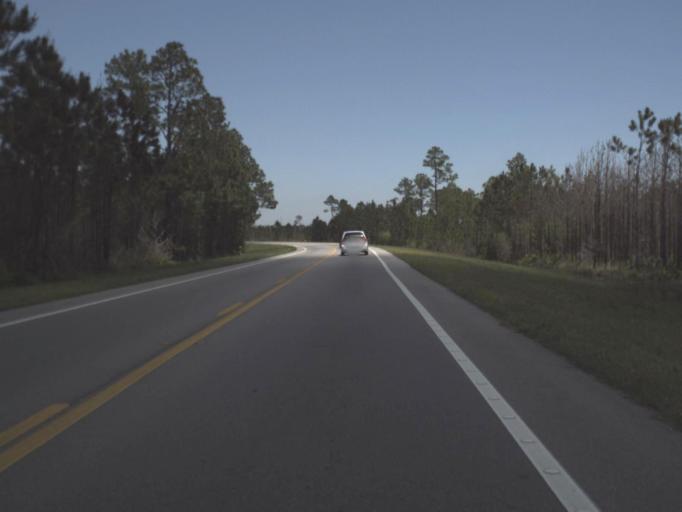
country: US
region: Florida
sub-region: Escambia County
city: Myrtle Grove
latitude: 30.3903
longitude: -87.3445
